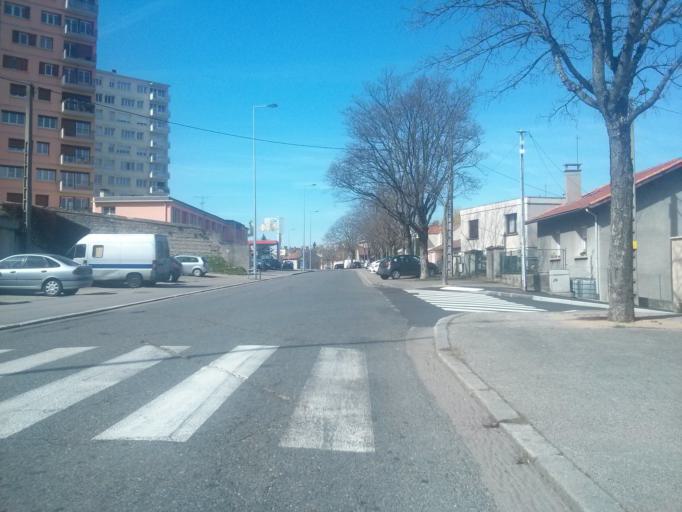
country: FR
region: Rhone-Alpes
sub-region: Departement de la Loire
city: Saint-Etienne
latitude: 45.4291
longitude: 4.4132
